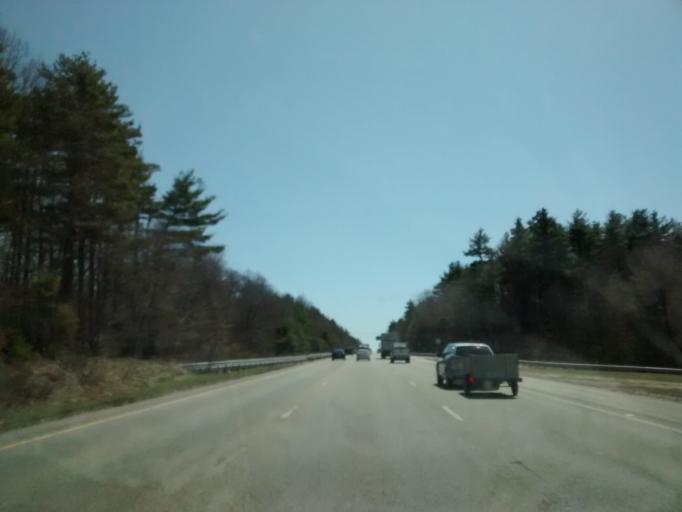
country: US
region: Massachusetts
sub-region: Middlesex County
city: Hopkinton
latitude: 42.2159
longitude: -71.5475
